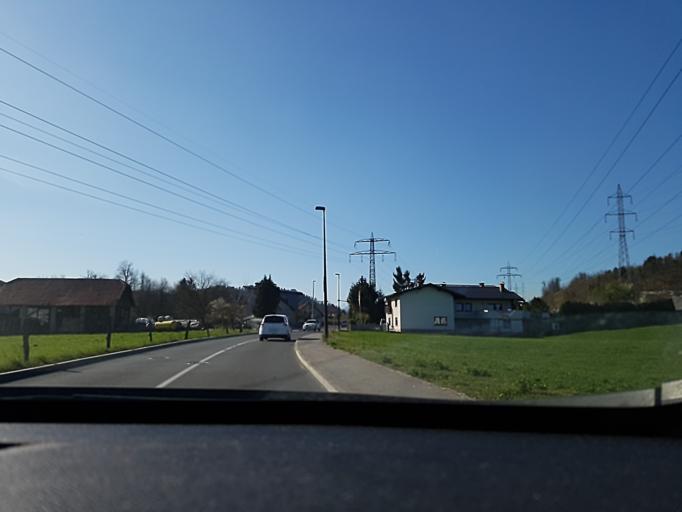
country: SI
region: Medvode
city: Zgornje Pirnice
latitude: 46.1182
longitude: 14.4529
